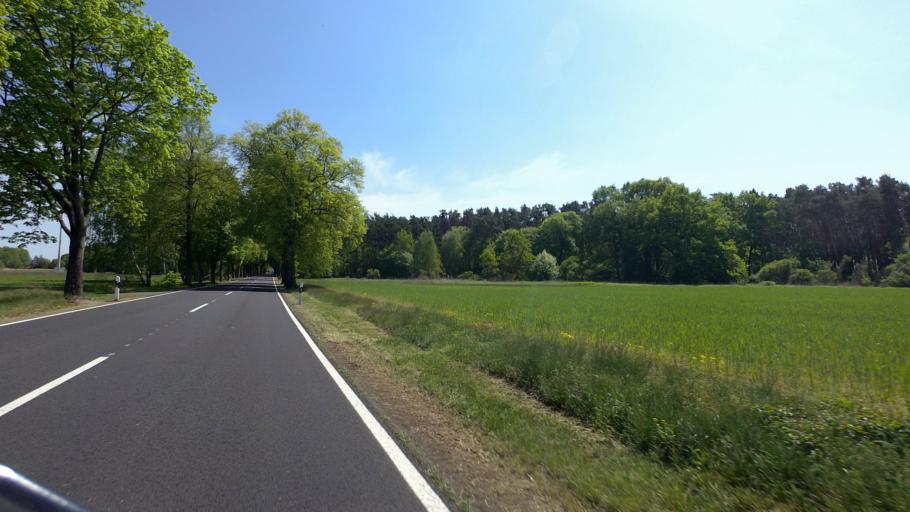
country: DE
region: Brandenburg
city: Munchehofe
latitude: 52.0901
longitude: 13.8591
